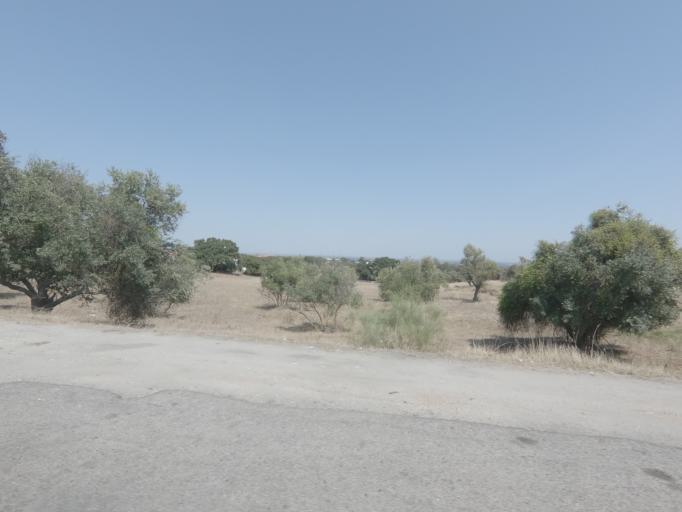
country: PT
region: Setubal
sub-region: Palmela
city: Palmela
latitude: 38.5667
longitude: -8.8878
